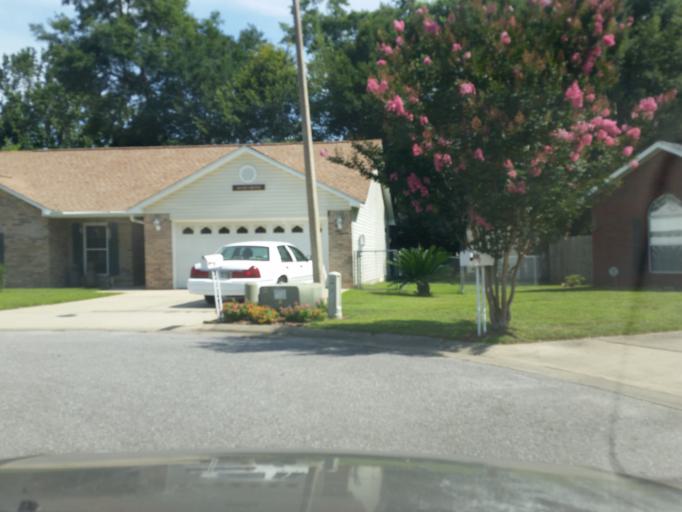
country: US
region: Florida
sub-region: Escambia County
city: Ferry Pass
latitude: 30.5145
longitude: -87.1934
